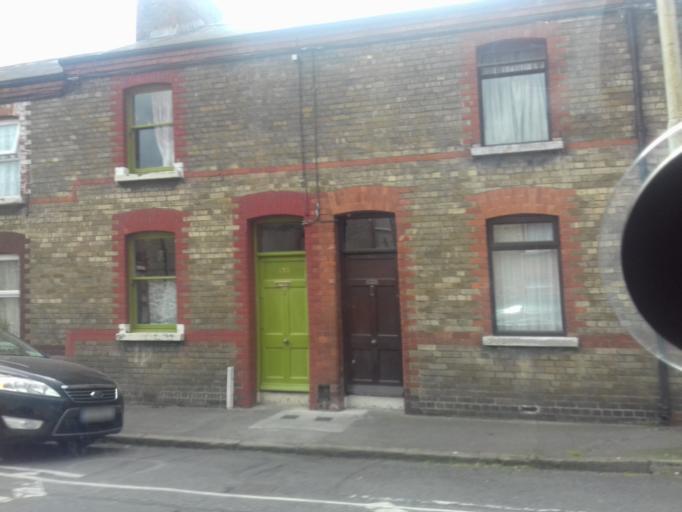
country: IE
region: Leinster
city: Cabra
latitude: 53.3525
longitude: -6.2893
